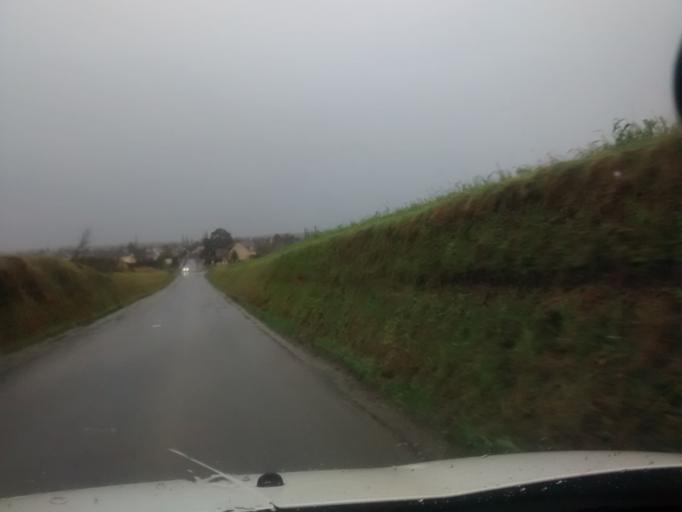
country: FR
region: Brittany
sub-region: Departement d'Ille-et-Vilaine
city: La Gouesniere
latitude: 48.5795
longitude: -1.8923
